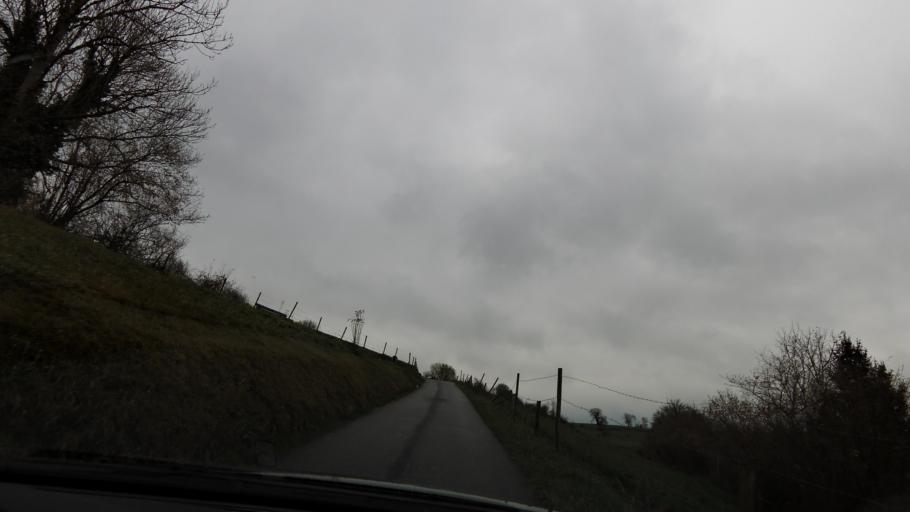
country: NL
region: Limburg
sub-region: Valkenburg aan de Geul
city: Schin op Geul
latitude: 50.8462
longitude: 5.8739
